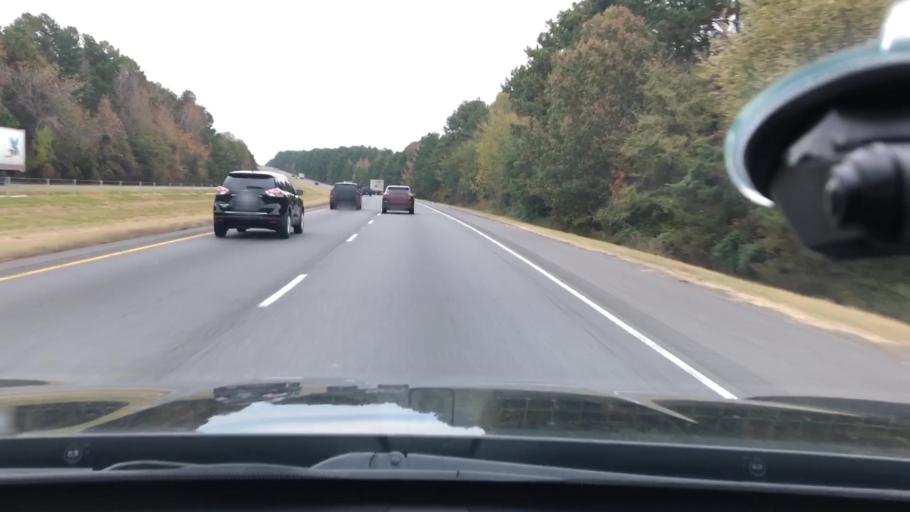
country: US
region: Arkansas
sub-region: Clark County
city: Gurdon
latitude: 34.0345
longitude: -93.1447
